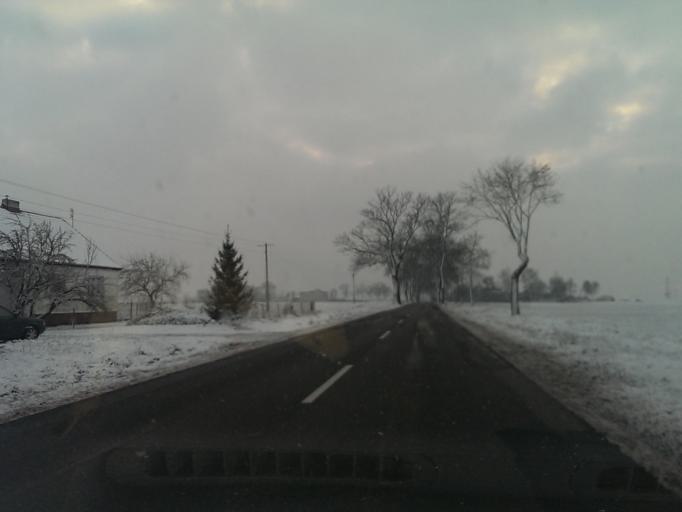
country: PL
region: Kujawsko-Pomorskie
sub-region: Powiat nakielski
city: Mrocza
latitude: 53.2085
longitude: 17.5873
